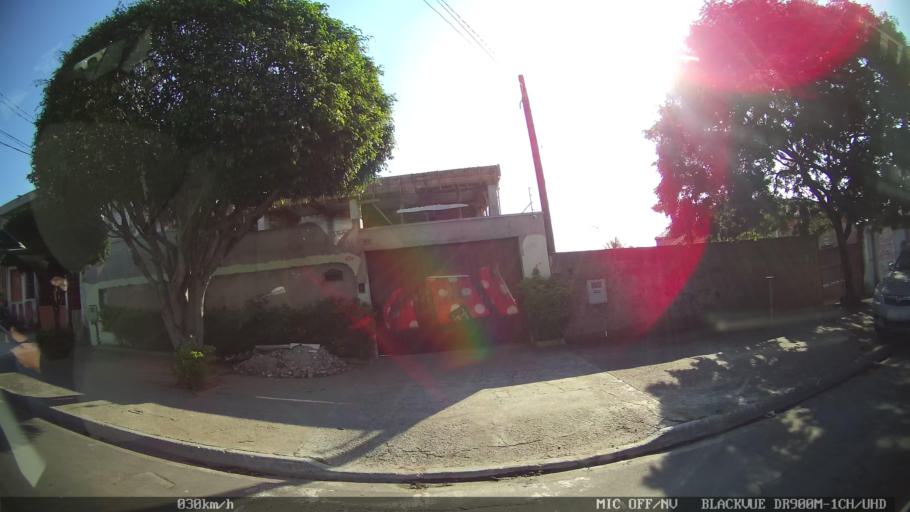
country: BR
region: Sao Paulo
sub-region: Indaiatuba
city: Indaiatuba
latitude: -22.9877
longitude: -47.1492
